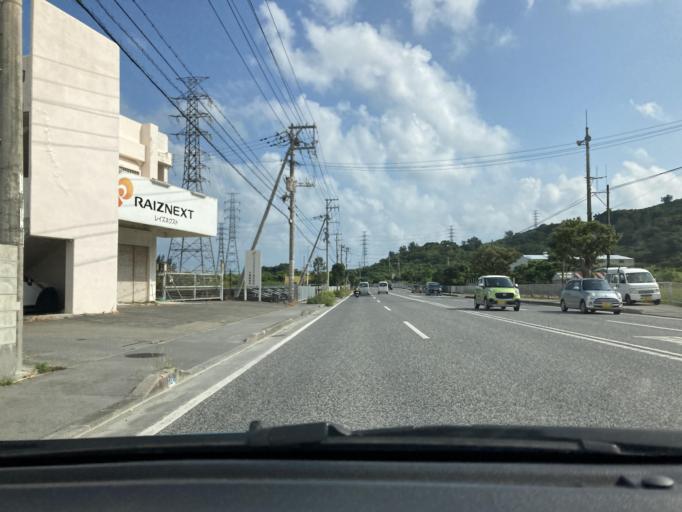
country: JP
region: Okinawa
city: Chatan
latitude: 26.2938
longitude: 127.8094
